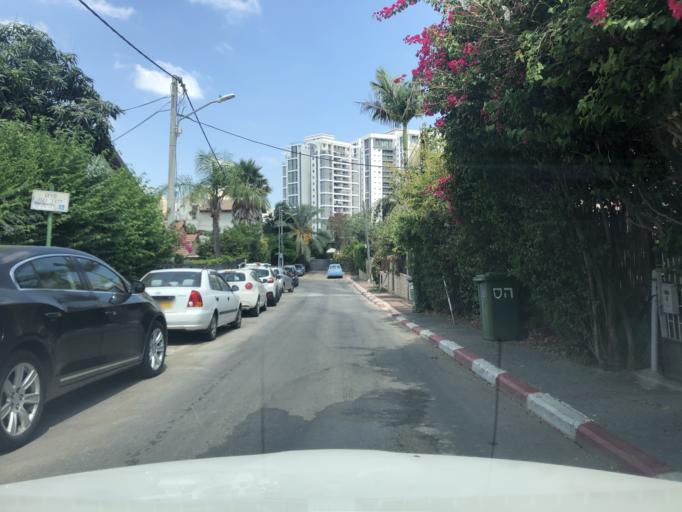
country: IL
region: Tel Aviv
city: Giv`at Shemu'el
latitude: 32.0657
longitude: 34.8489
